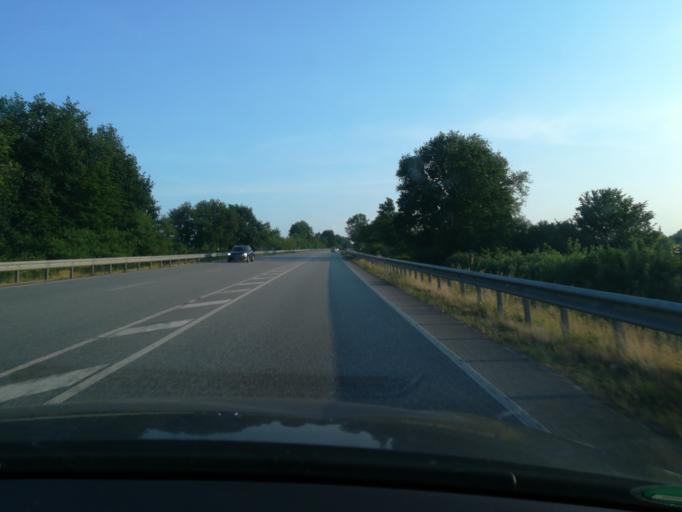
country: DE
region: Schleswig-Holstein
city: Trittau
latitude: 53.6059
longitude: 10.3814
